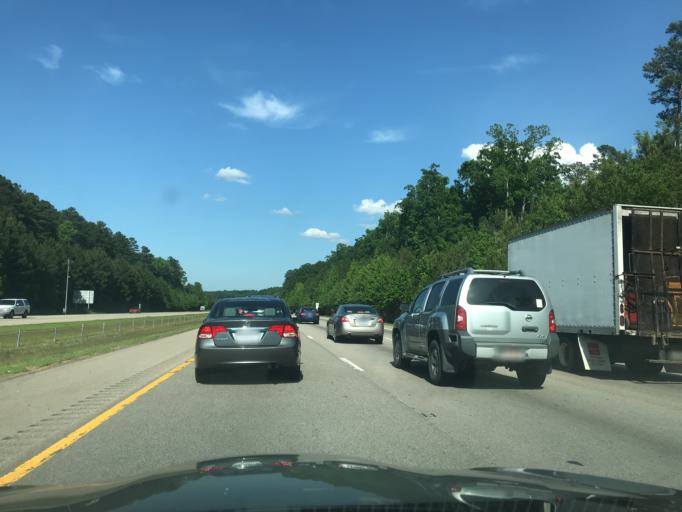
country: US
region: North Carolina
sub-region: Wake County
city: Cary
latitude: 35.9126
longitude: -78.7194
